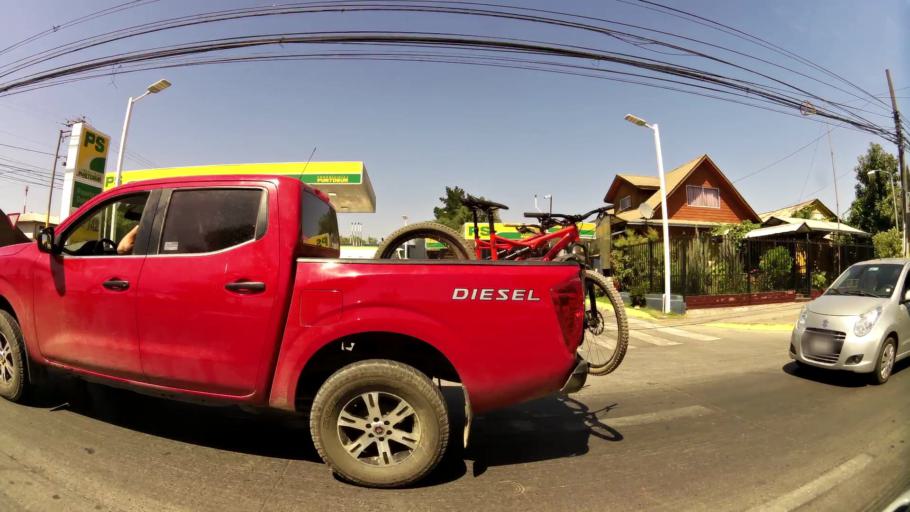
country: CL
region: Maule
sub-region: Provincia de Talca
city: Talca
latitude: -35.4298
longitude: -71.6334
